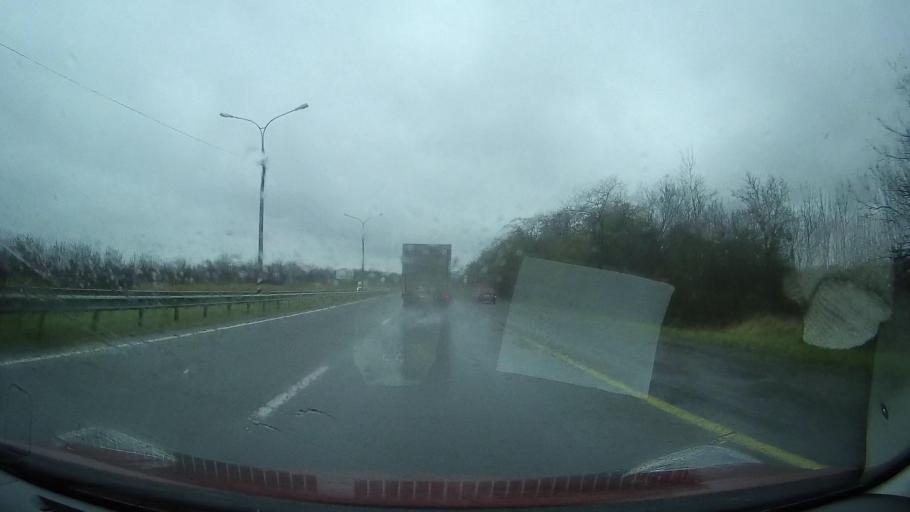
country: RU
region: Stavropol'skiy
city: Nevinnomyssk
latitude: 44.6379
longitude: 41.9857
